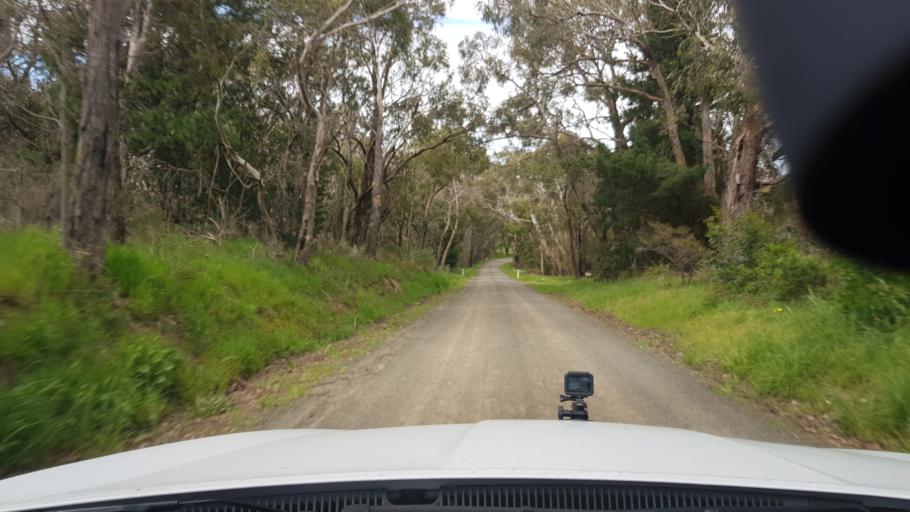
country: AU
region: Victoria
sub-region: Latrobe
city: Moe
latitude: -38.1615
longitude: 146.1354
